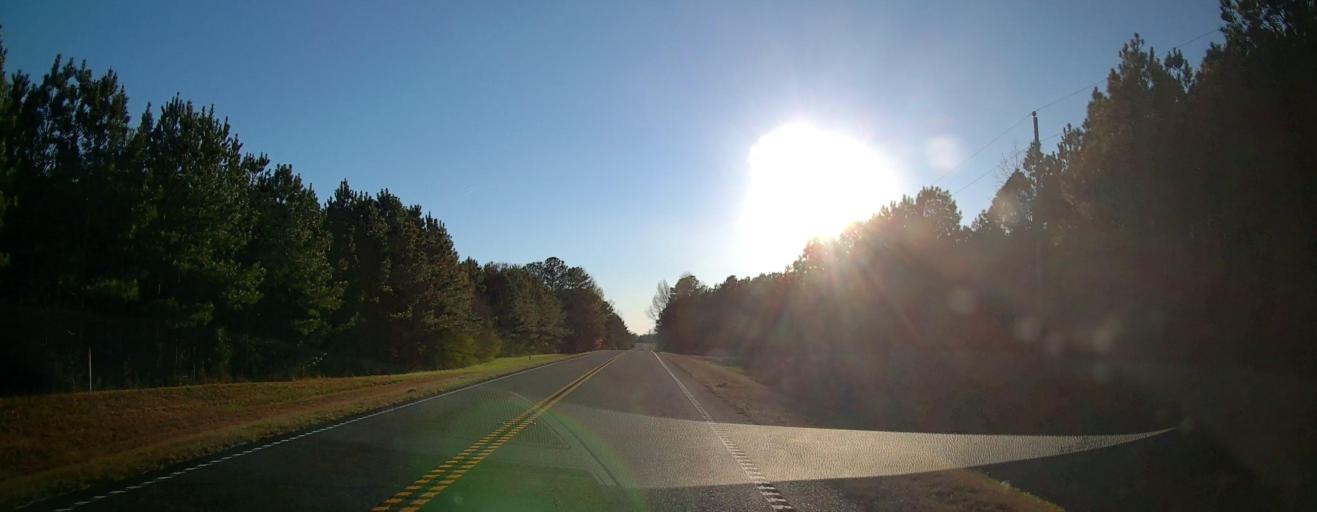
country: US
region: Georgia
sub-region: Talbot County
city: Talbotton
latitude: 32.6593
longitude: -84.6565
